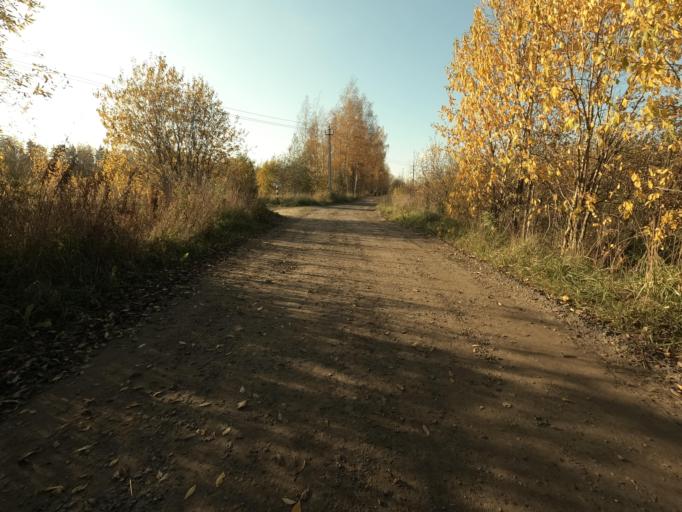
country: RU
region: Leningrad
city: Sertolovo
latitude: 60.1462
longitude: 30.2404
